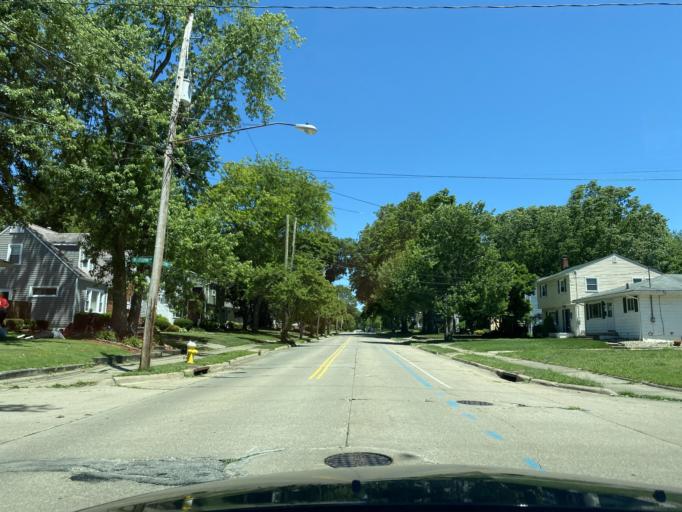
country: US
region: Ohio
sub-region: Summit County
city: Fairlawn
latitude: 41.1191
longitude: -81.5765
